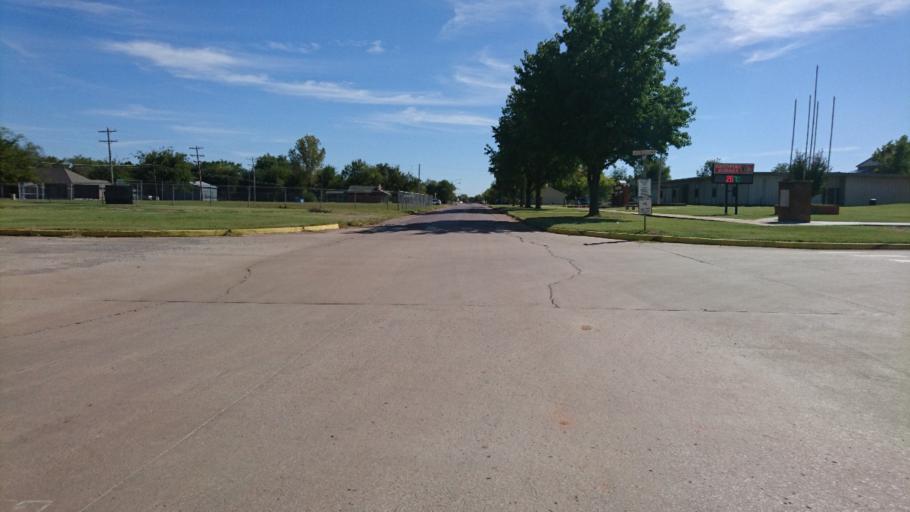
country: US
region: Oklahoma
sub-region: Lincoln County
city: Stroud
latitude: 35.7092
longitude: -96.7652
